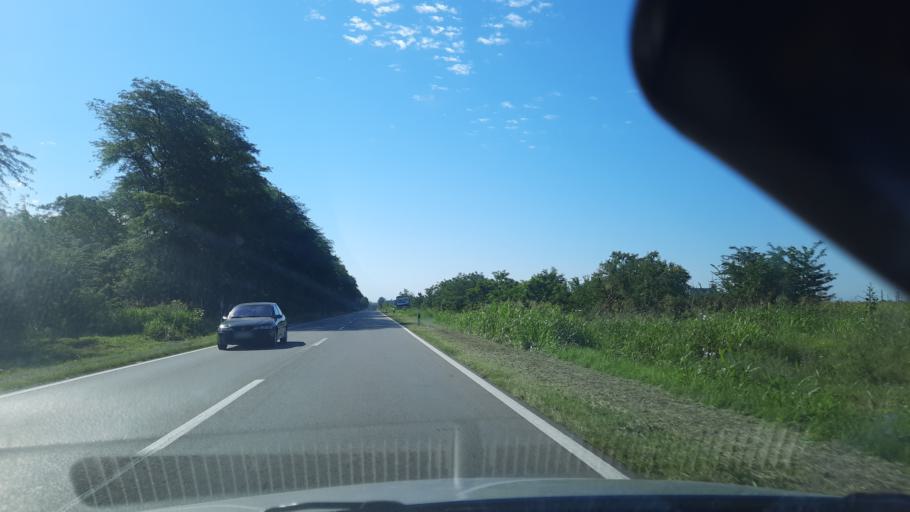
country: RS
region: Autonomna Pokrajina Vojvodina
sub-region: Juznobanatski Okrug
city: Kovin
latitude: 44.7597
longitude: 20.9596
